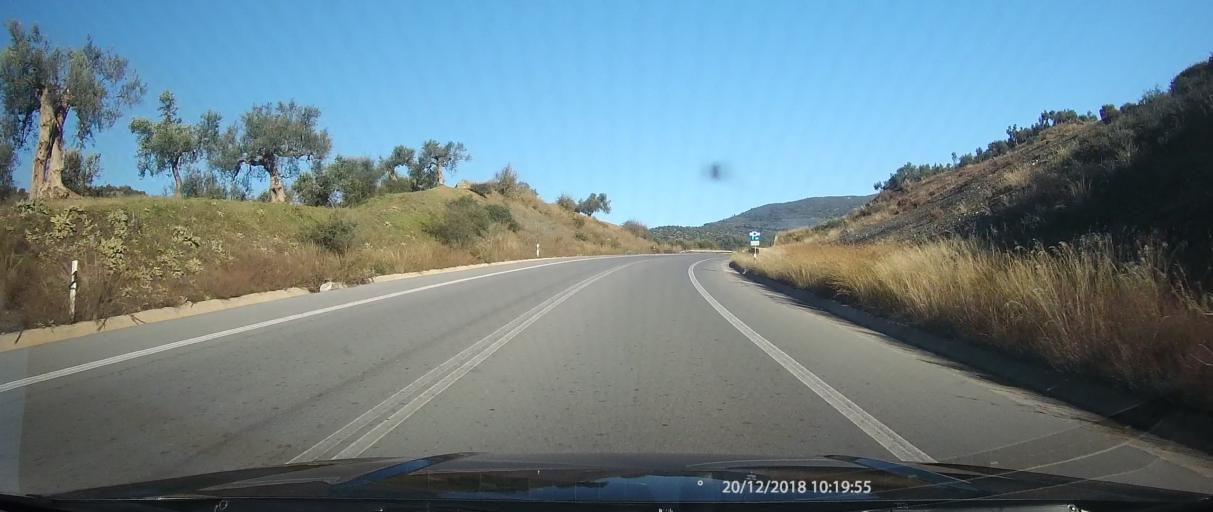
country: GR
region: Peloponnese
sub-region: Nomos Lakonias
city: Magoula
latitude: 37.1420
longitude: 22.4248
